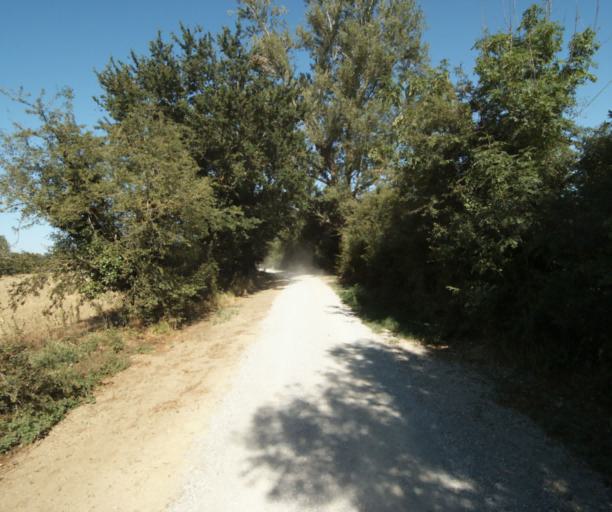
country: FR
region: Midi-Pyrenees
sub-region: Departement du Tarn
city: Soreze
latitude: 43.4594
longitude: 2.0399
